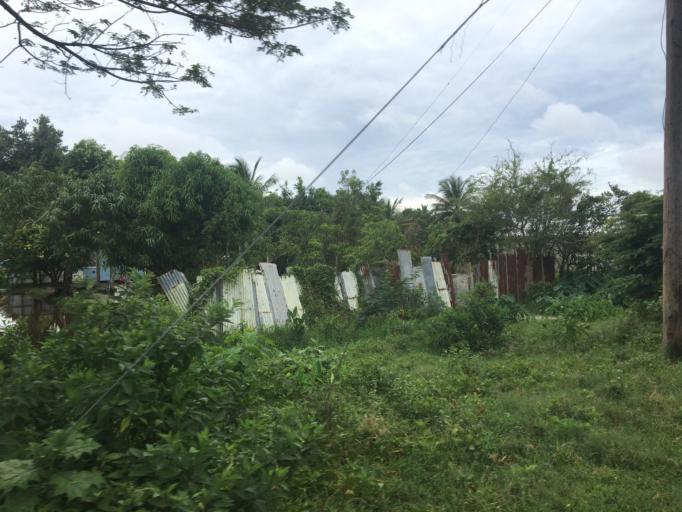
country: GY
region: Demerara-Mahaica
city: Georgetown
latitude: 6.7951
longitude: -58.1323
